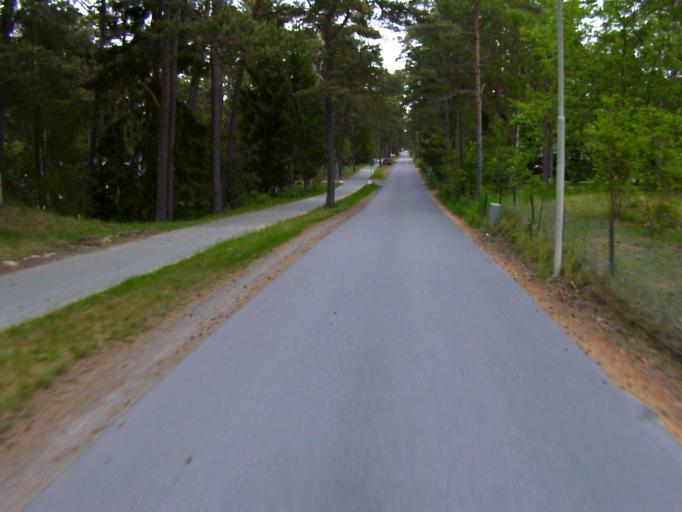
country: SE
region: Skane
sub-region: Kristianstads Kommun
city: Ahus
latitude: 55.9430
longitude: 14.3196
